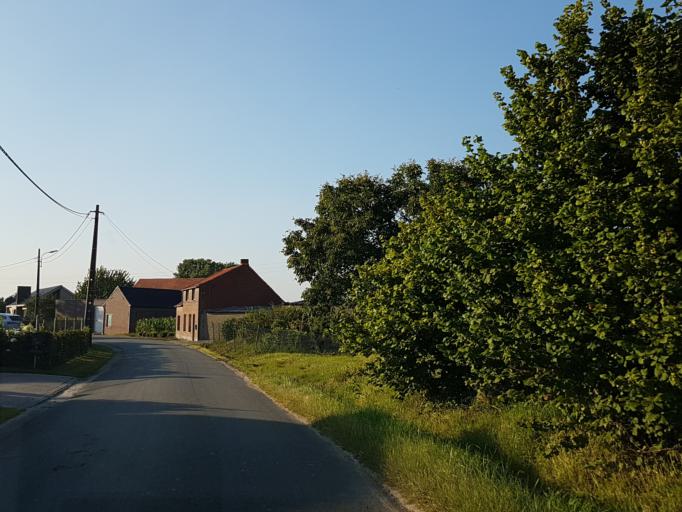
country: BE
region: Flanders
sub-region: Provincie Vlaams-Brabant
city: Opwijk
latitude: 50.9511
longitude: 4.2019
